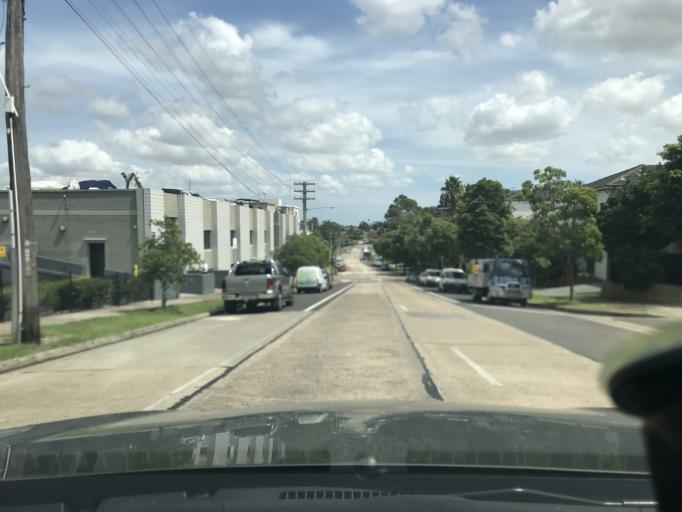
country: AU
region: New South Wales
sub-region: Canada Bay
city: Wareemba
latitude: -33.8499
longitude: 151.1381
